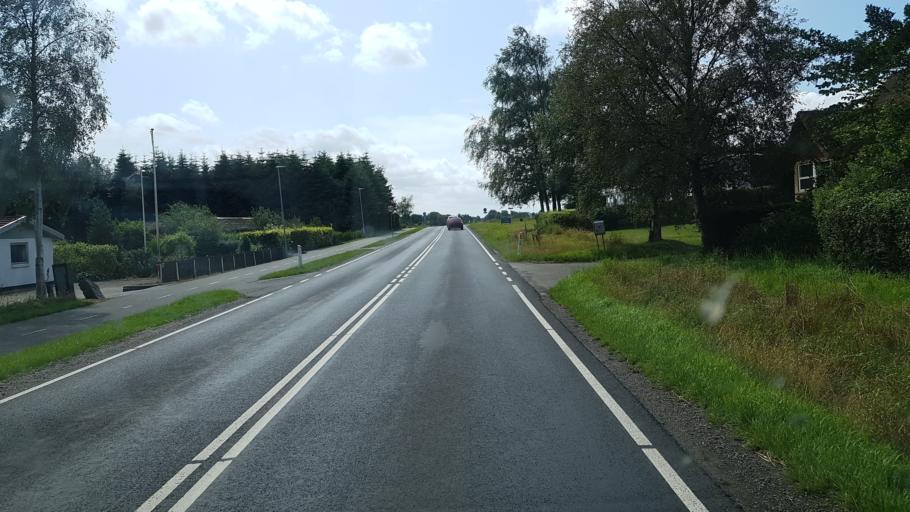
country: DK
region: South Denmark
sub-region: Vejen Kommune
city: Vejen
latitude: 55.5623
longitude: 9.1287
